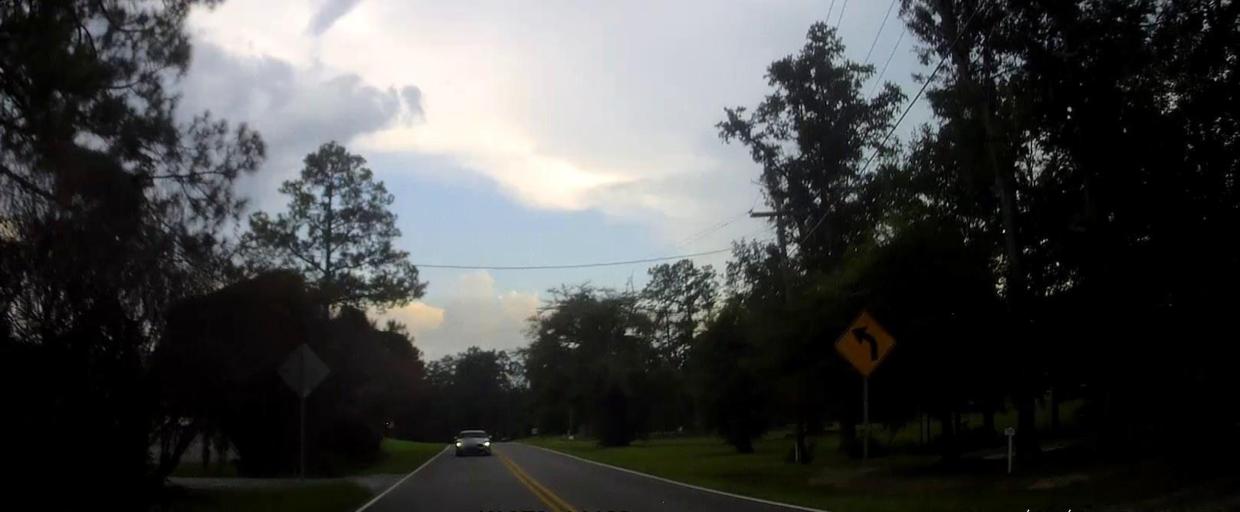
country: US
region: Georgia
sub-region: Laurens County
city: East Dublin
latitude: 32.5942
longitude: -82.8982
